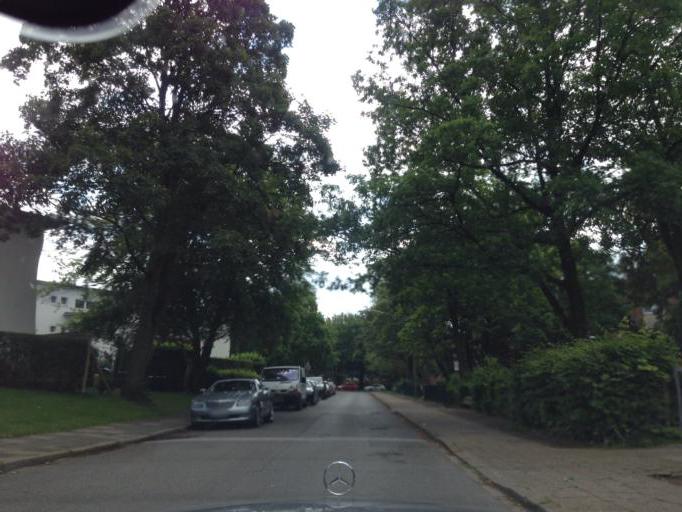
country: DE
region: Schleswig-Holstein
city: Barsbuettel
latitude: 53.5841
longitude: 10.1509
